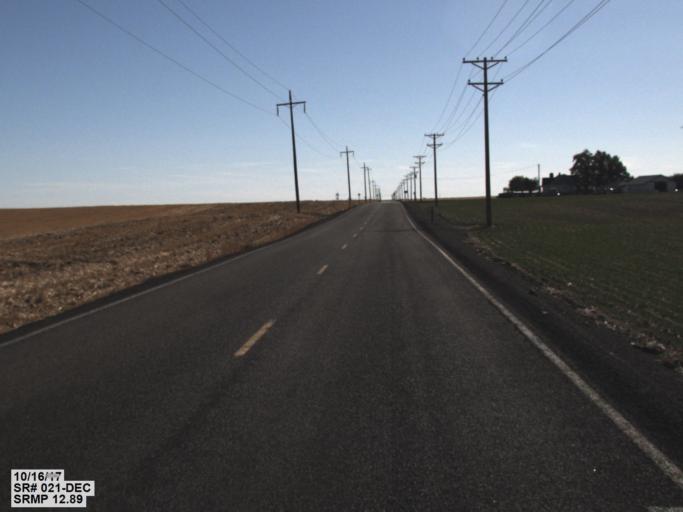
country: US
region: Washington
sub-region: Franklin County
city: Connell
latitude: 46.8129
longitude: -118.5473
